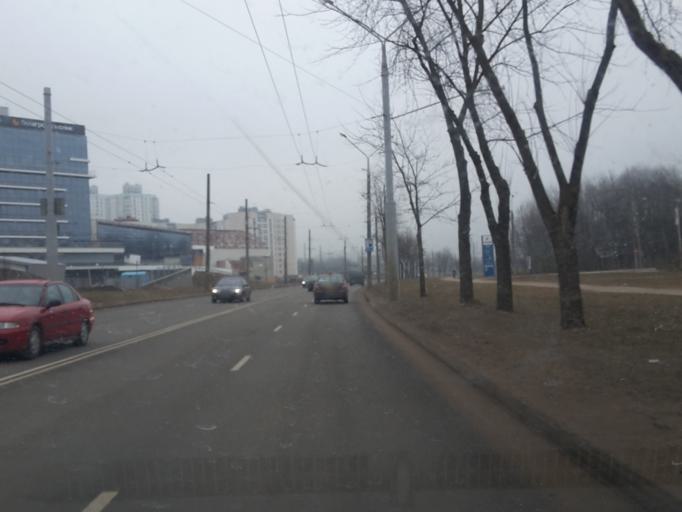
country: BY
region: Minsk
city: Novoye Medvezhino
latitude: 53.8913
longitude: 27.4581
